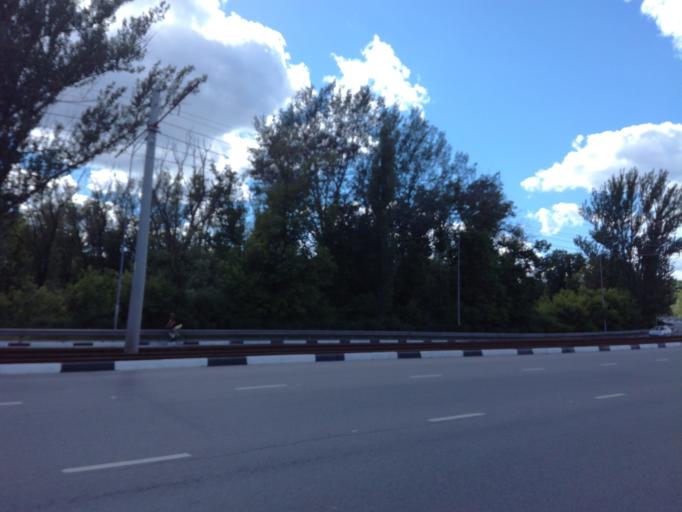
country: RU
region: Kursk
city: Kursk
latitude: 51.7554
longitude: 36.2102
